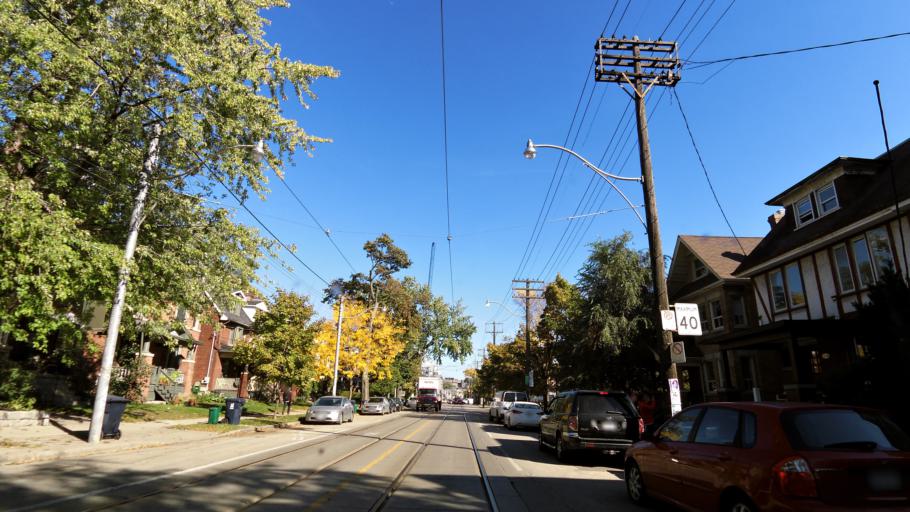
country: CA
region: Ontario
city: Toronto
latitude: 43.6512
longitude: -79.4532
